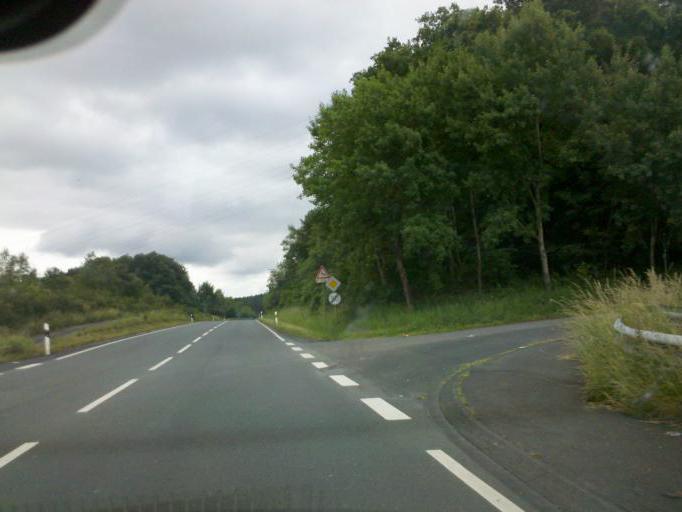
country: DE
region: North Rhine-Westphalia
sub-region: Regierungsbezirk Arnsberg
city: Siegen
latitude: 50.8679
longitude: 8.0473
